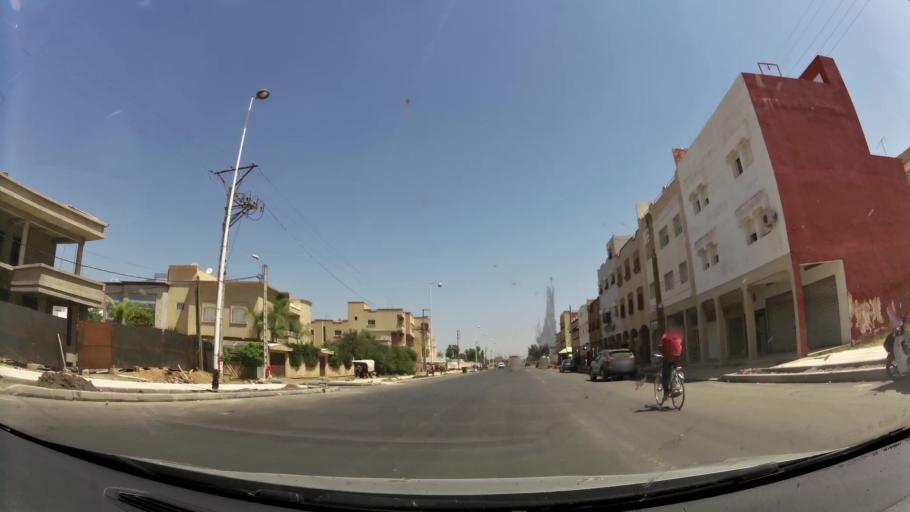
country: MA
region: Rabat-Sale-Zemmour-Zaer
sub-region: Khemisset
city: Khemisset
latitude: 33.8129
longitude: -6.0758
